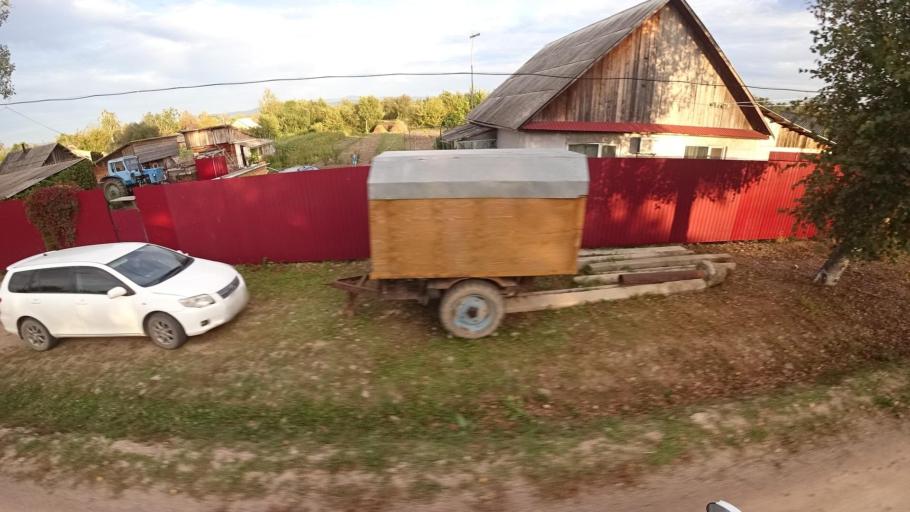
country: RU
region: Primorskiy
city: Yakovlevka
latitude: 44.4253
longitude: 133.4811
